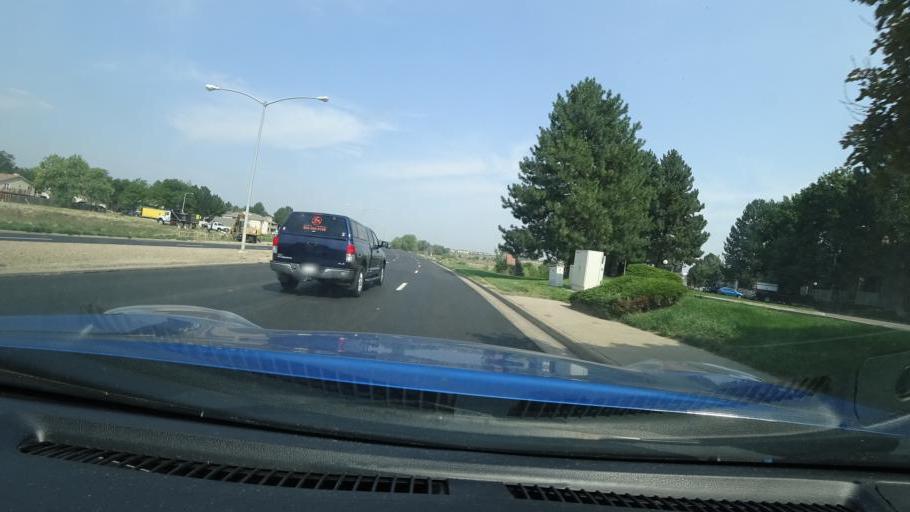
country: US
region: Colorado
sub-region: Adams County
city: Aurora
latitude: 39.7029
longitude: -104.7753
